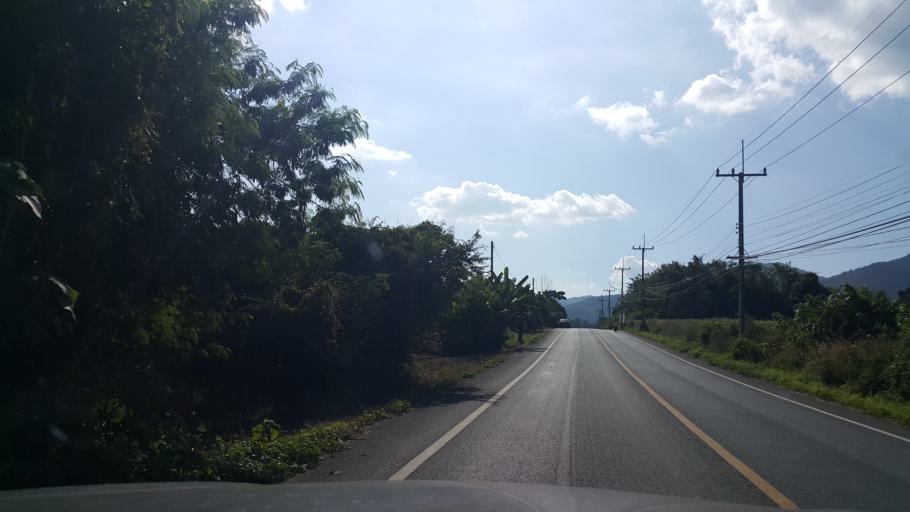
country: TH
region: Lamphun
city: Mae Tha
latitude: 18.5200
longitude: 99.2253
